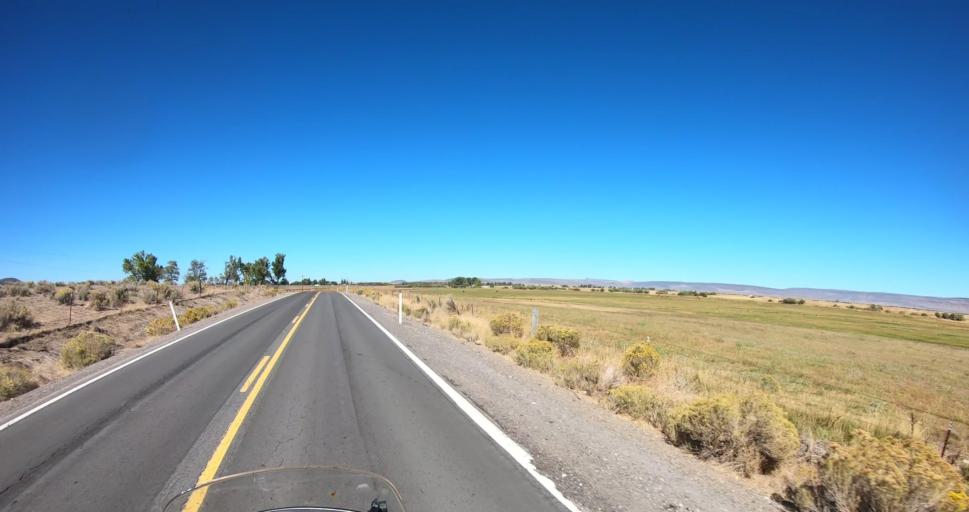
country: US
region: Oregon
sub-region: Lake County
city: Lakeview
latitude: 42.6731
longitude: -120.5271
